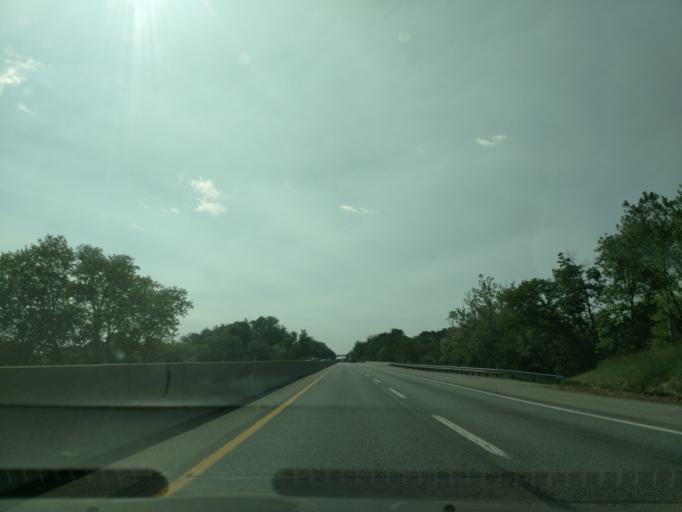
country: US
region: Pennsylvania
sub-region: Lancaster County
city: Denver
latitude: 40.2408
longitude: -76.1396
